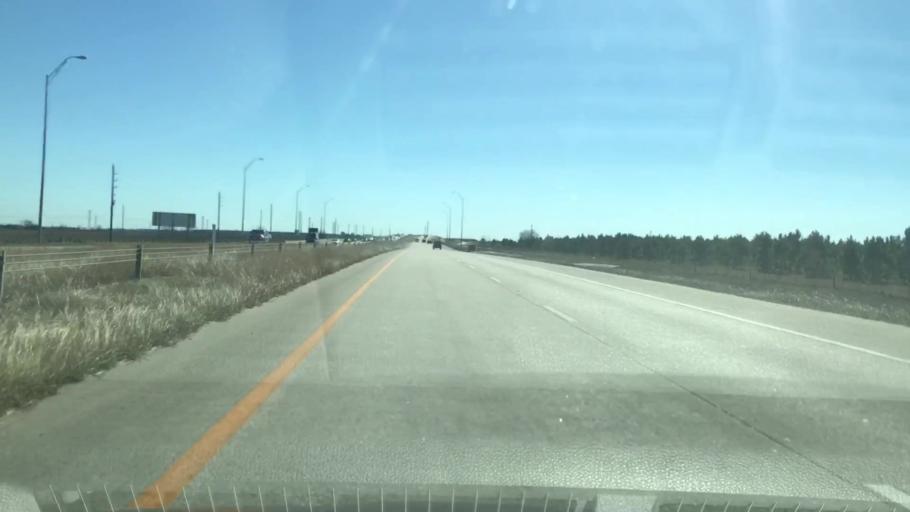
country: US
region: Texas
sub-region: Harris County
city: Cypress
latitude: 29.9302
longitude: -95.7632
